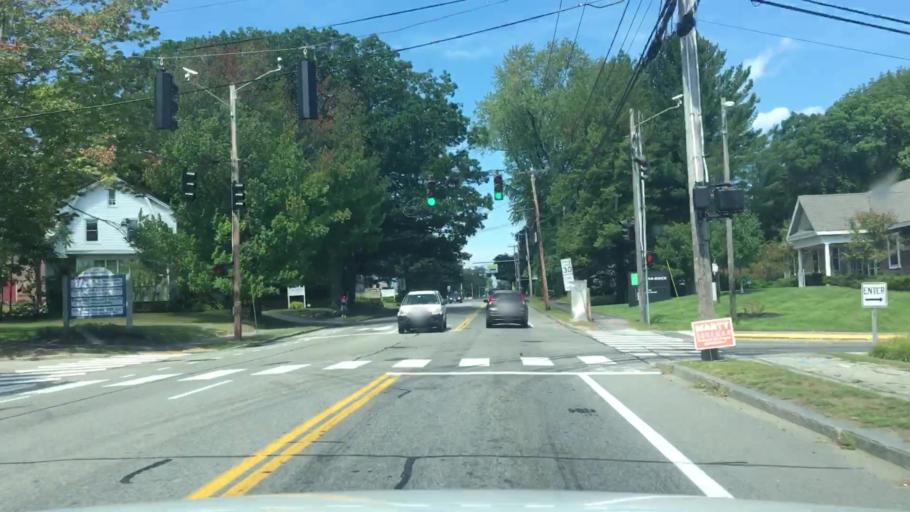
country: US
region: Maine
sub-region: Cumberland County
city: Falmouth
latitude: 43.7043
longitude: -70.2896
